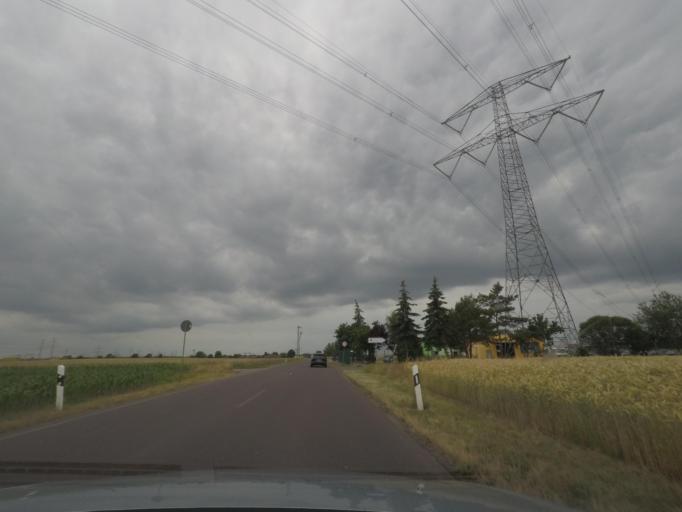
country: DE
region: Saxony-Anhalt
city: Wolmirstedt
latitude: 52.2761
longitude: 11.6438
